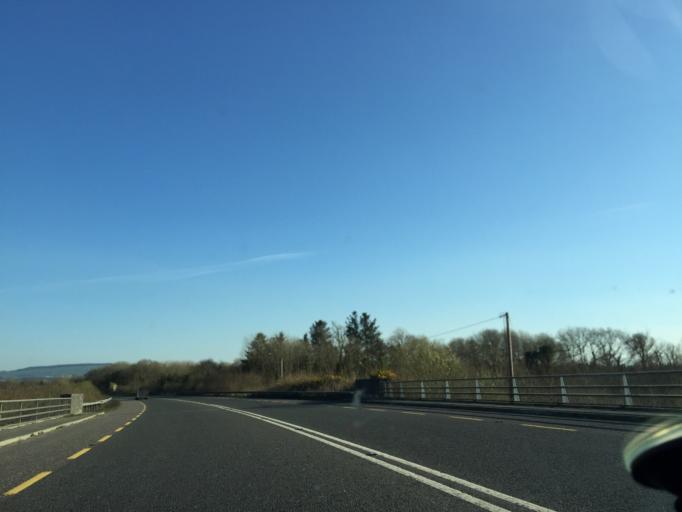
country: IE
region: Munster
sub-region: Ciarrai
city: Castleisland
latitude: 52.1975
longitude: -9.5709
